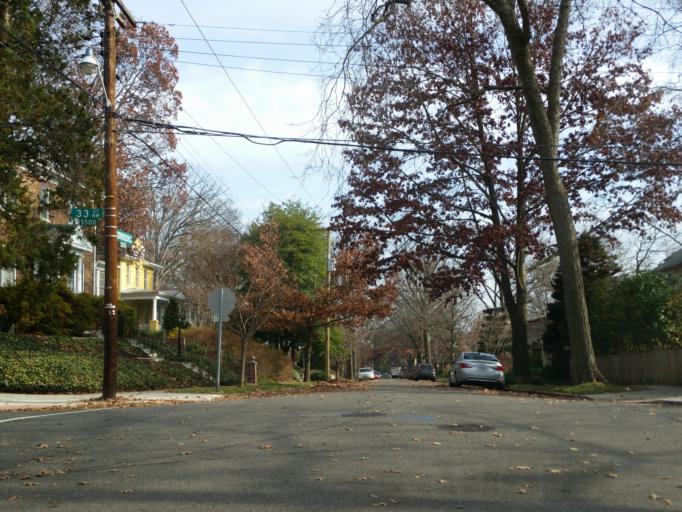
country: US
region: Maryland
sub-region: Montgomery County
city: Chevy Chase
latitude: 38.9640
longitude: -77.0665
